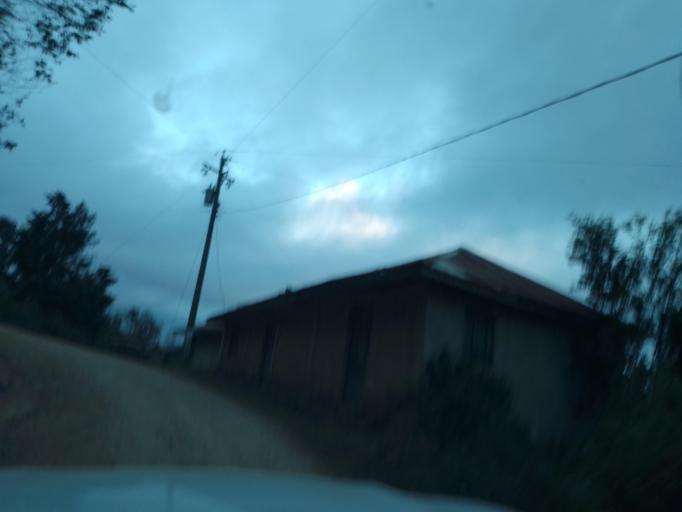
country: MX
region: Chiapas
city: Motozintla de Mendoza
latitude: 15.2201
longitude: -92.2362
